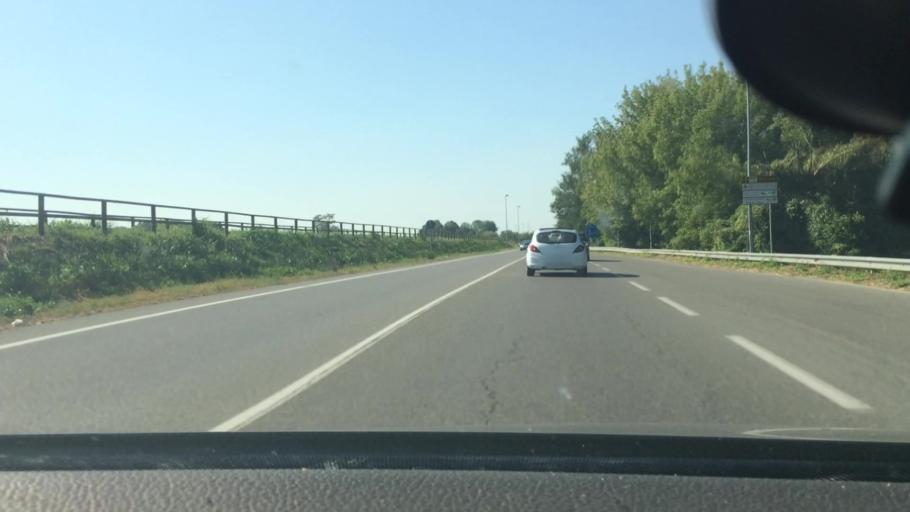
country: IT
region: Lombardy
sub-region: Provincia di Lodi
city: San Rocco al Porto
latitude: 45.0734
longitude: 9.7073
